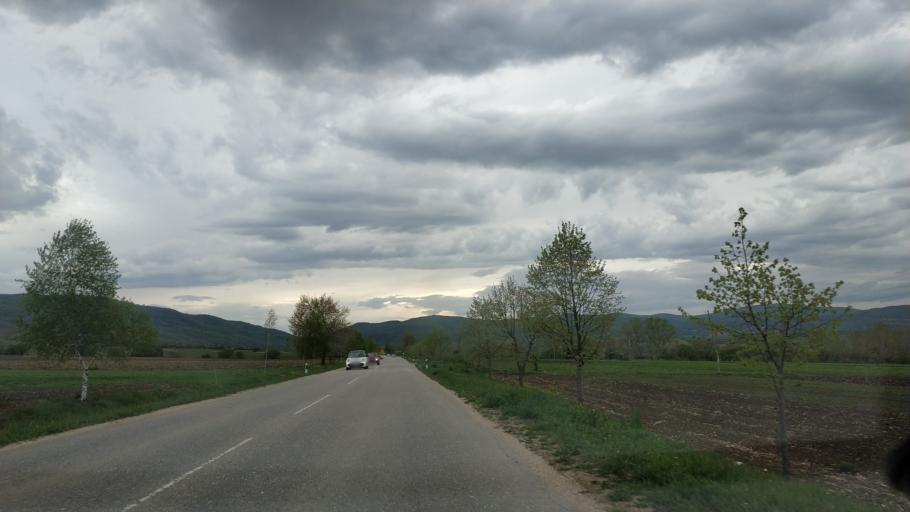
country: RS
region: Central Serbia
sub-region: Zajecarski Okrug
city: Soko Banja
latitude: 43.6565
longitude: 21.8136
